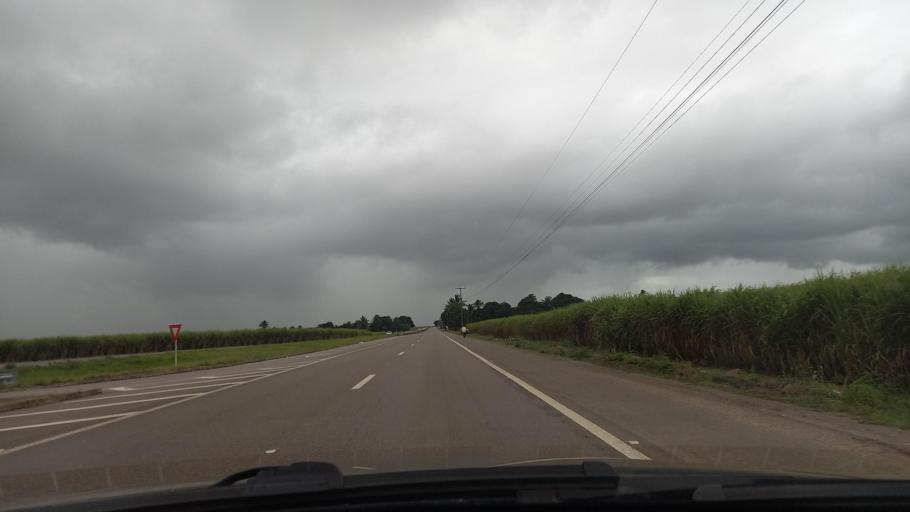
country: BR
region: Alagoas
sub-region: Limoeiro De Anadia
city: Cajueiro
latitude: -9.7627
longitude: -36.4329
